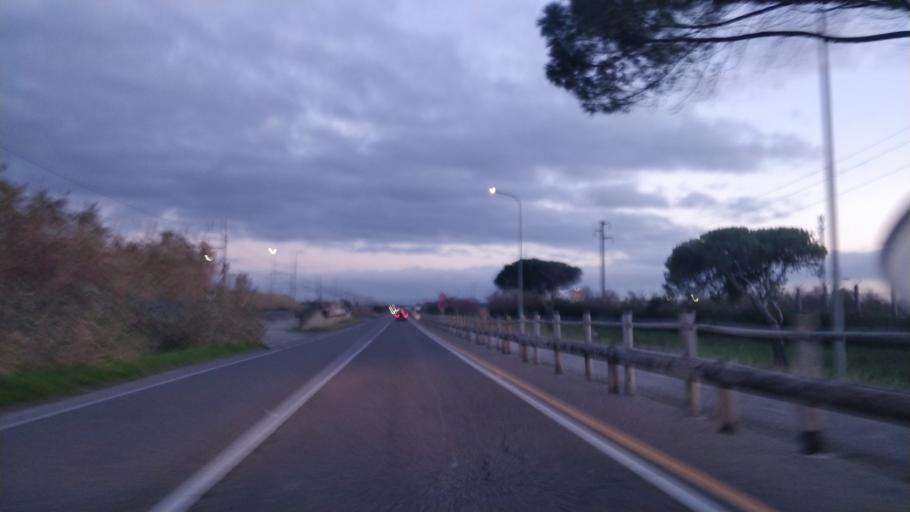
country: IT
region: Tuscany
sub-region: Provincia di Livorno
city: Rosignano Solvay-Castiglioncello
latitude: 43.3811
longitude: 10.4432
